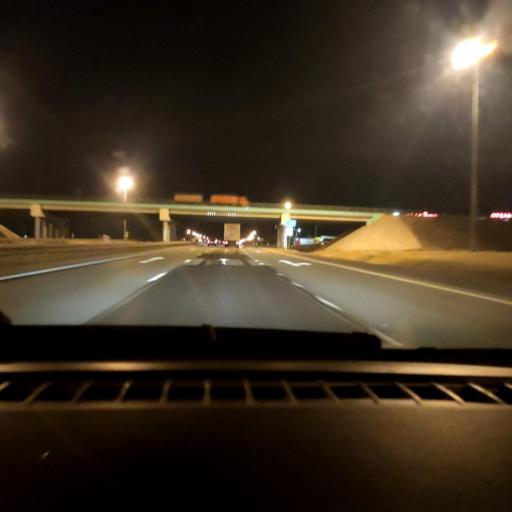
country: RU
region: Lipetsk
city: Khlevnoye
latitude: 52.1199
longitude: 39.1908
